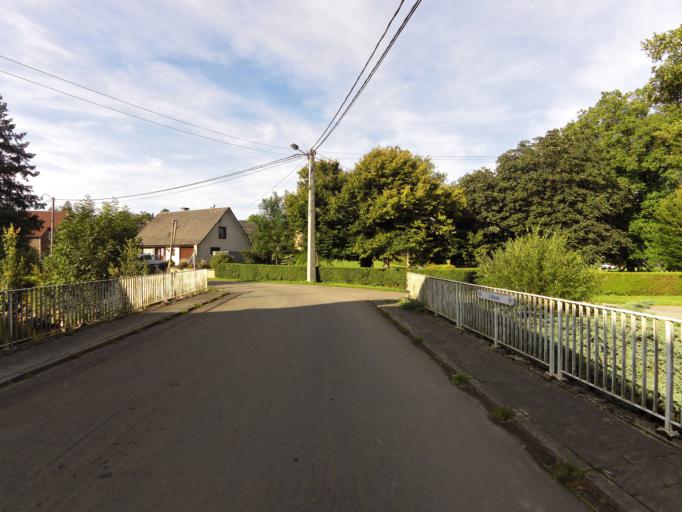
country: BE
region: Wallonia
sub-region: Province du Luxembourg
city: Erezee
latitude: 50.2676
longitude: 5.5616
